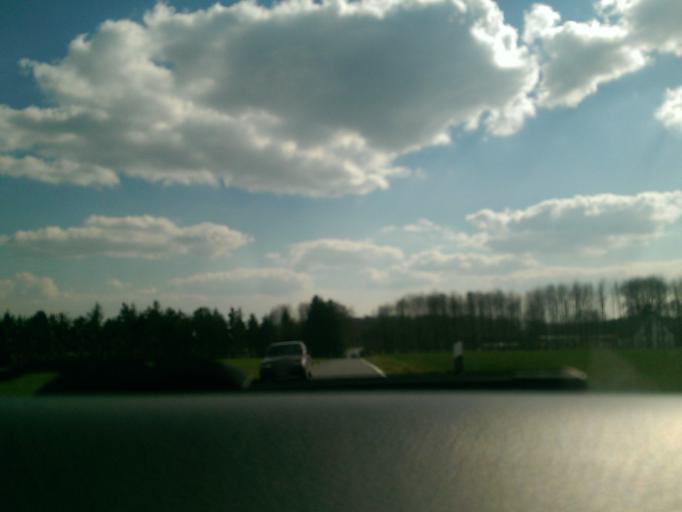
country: DE
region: North Rhine-Westphalia
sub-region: Regierungsbezirk Munster
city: Muenster
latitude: 51.9457
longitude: 7.6778
